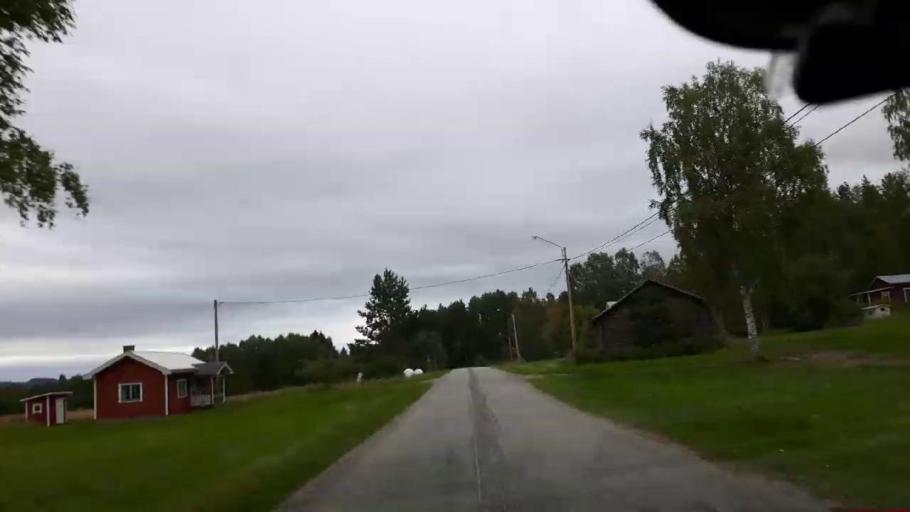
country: SE
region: Vaesternorrland
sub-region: Ange Kommun
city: Fransta
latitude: 62.7717
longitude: 16.0036
